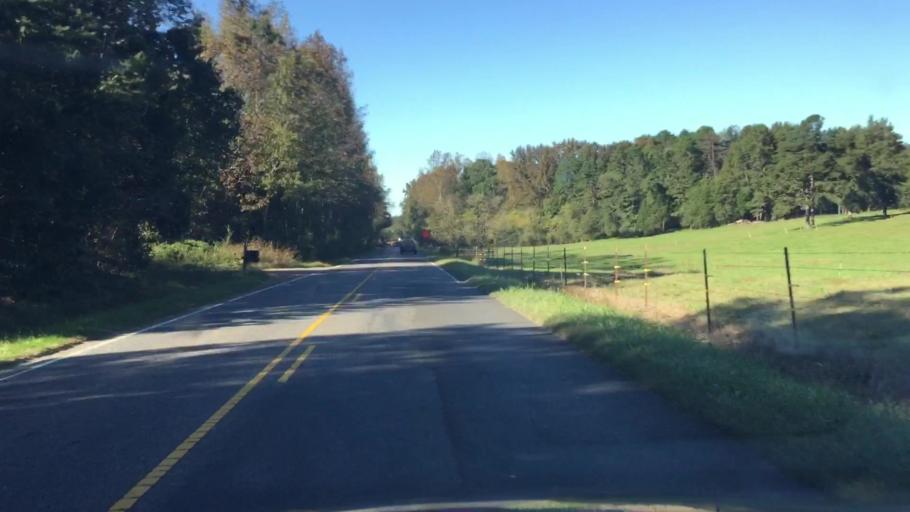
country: US
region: North Carolina
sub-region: Gaston County
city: Davidson
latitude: 35.5115
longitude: -80.7690
